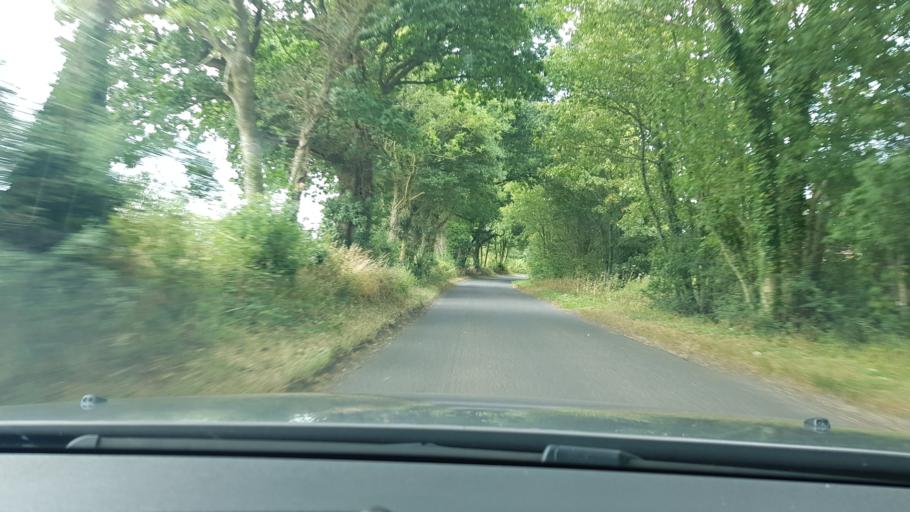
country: GB
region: England
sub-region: Wiltshire
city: Shalbourne
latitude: 51.3647
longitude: -1.5712
